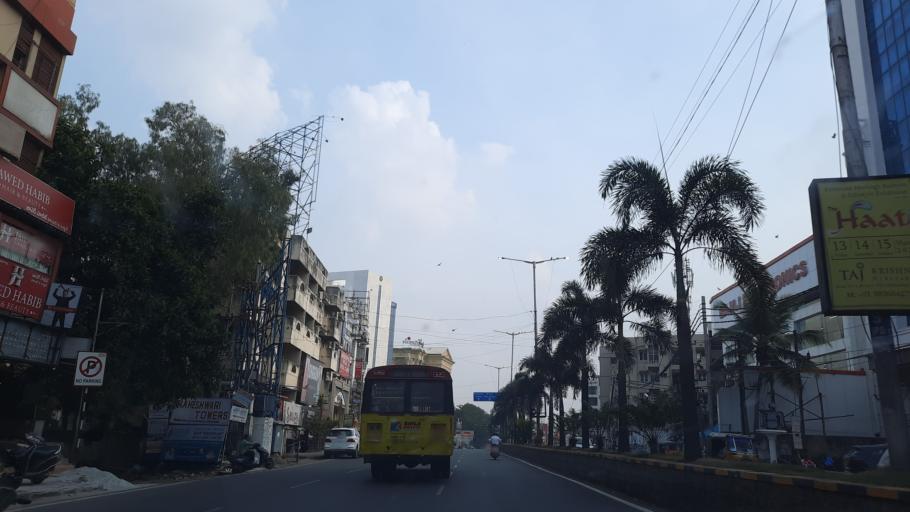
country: IN
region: Telangana
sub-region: Hyderabad
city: Hyderabad
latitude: 17.4094
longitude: 78.4503
